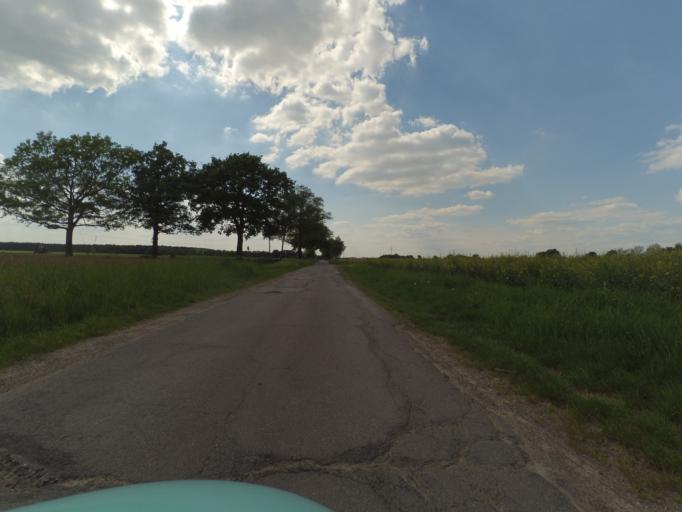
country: DE
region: Lower Saxony
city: Dollbergen
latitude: 52.4511
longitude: 10.1534
